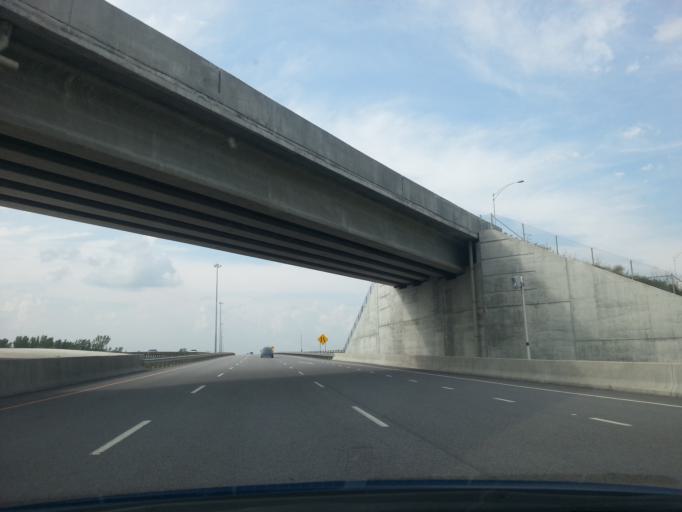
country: CA
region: Quebec
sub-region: Monteregie
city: Vaudreuil-Dorion
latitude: 45.3613
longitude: -74.0480
